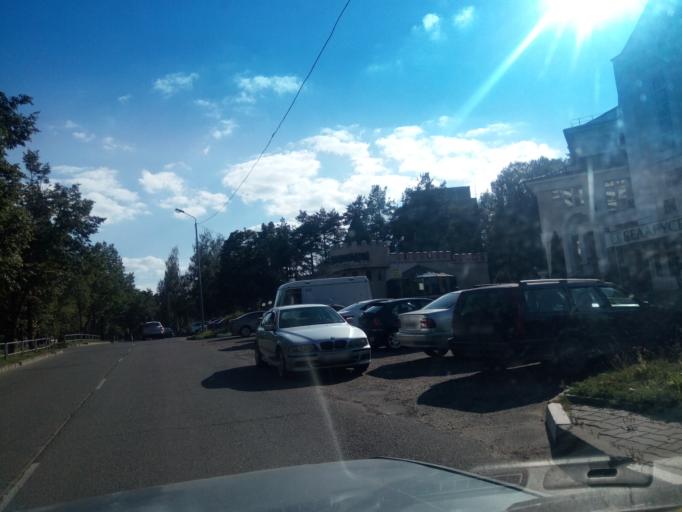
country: BY
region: Vitebsk
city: Navapolatsk
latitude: 55.5264
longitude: 28.6692
